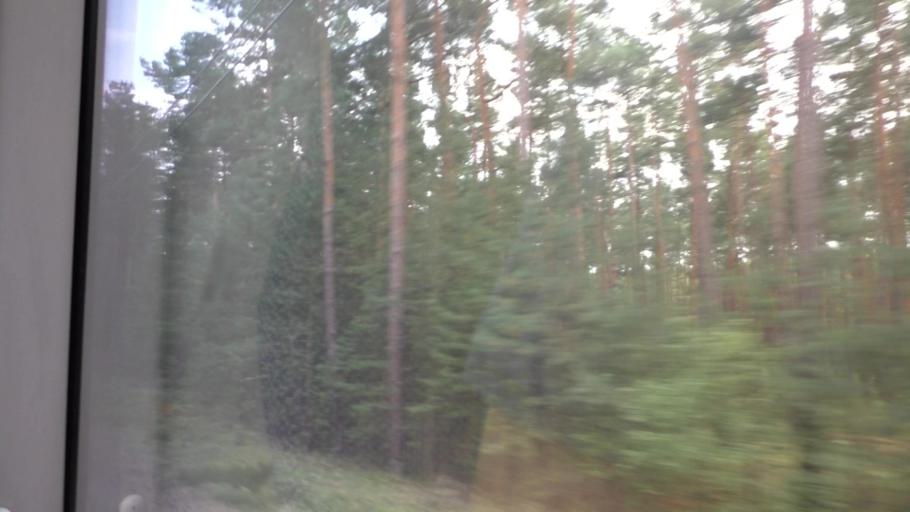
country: DE
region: Brandenburg
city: Reichenwalde
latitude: 52.2262
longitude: 13.9742
